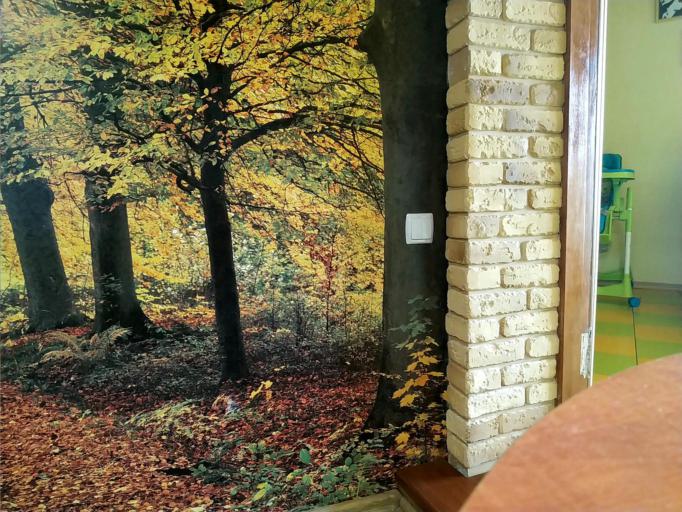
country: RU
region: Smolensk
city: Ozernyy
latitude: 55.4622
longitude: 32.6654
